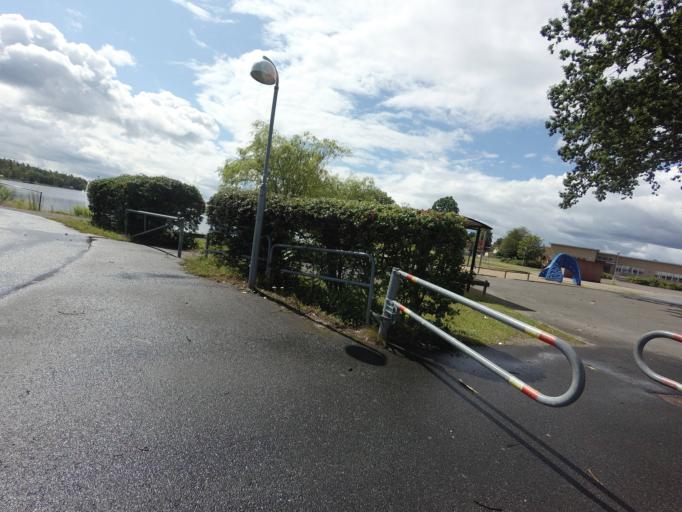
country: SE
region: Skane
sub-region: Osby Kommun
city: Osby
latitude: 56.3788
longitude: 13.9986
